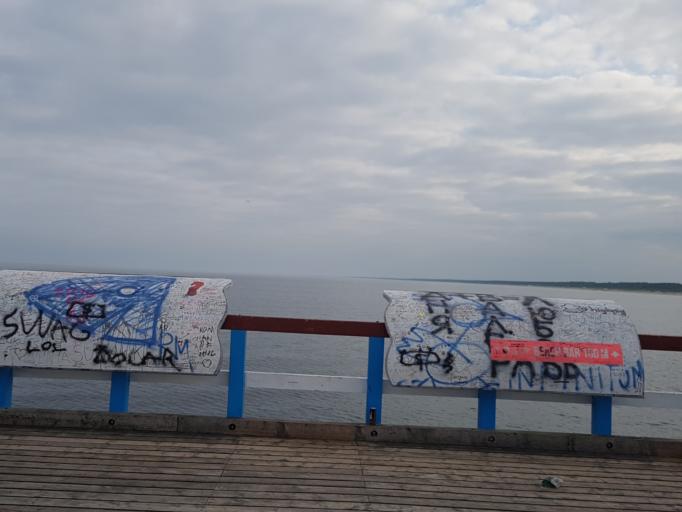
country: LT
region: Klaipedos apskritis
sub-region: Klaipeda
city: Palanga
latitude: 55.9212
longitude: 21.0445
